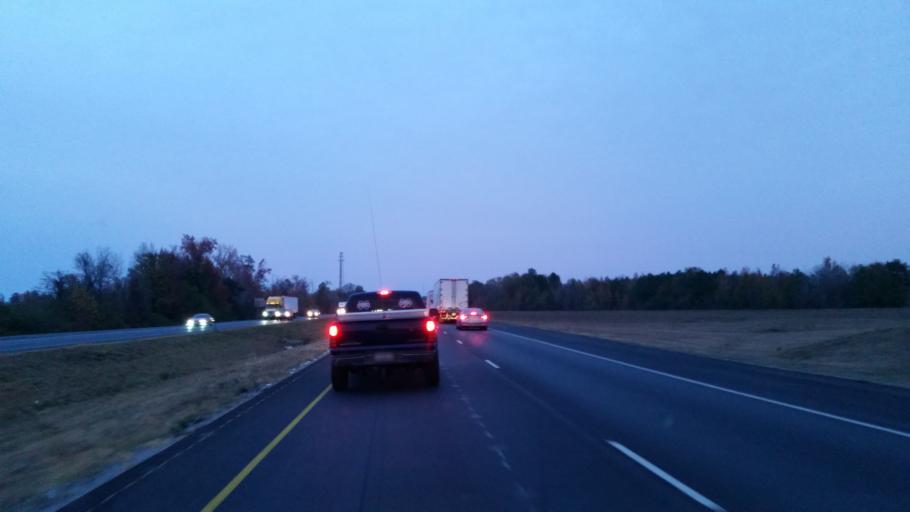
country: US
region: Alabama
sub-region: Tuscaloosa County
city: Tuscaloosa
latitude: 33.1533
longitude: -87.5963
